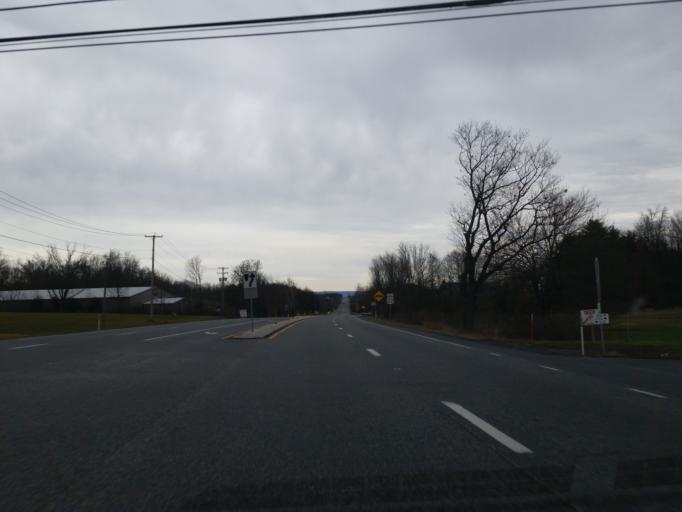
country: US
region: Pennsylvania
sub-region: Dauphin County
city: Skyline View
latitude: 40.3591
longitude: -76.6724
